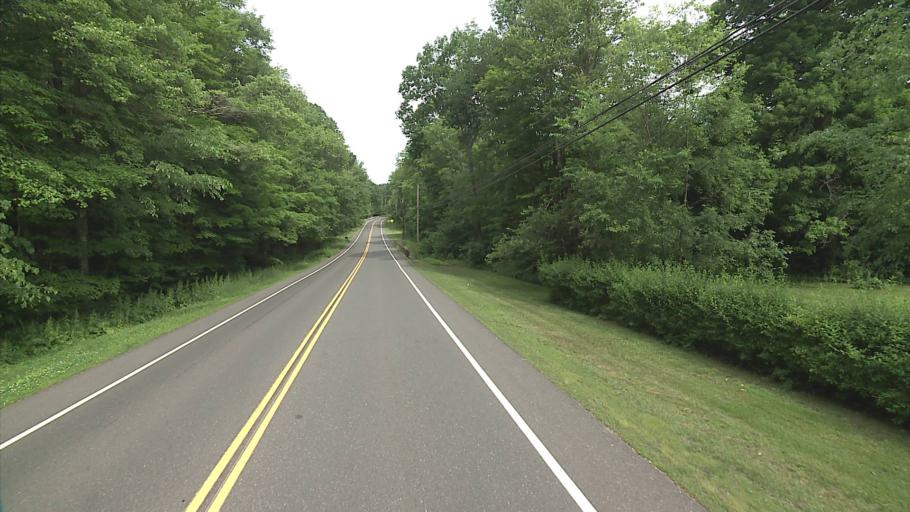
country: US
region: Connecticut
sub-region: Litchfield County
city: Bethlehem Village
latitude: 41.6703
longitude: -73.1684
